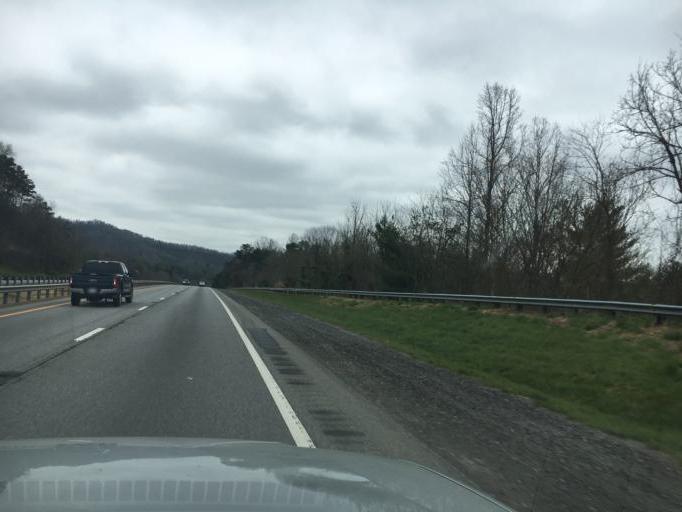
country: US
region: North Carolina
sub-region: Buncombe County
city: Weaverville
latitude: 35.7487
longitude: -82.5458
